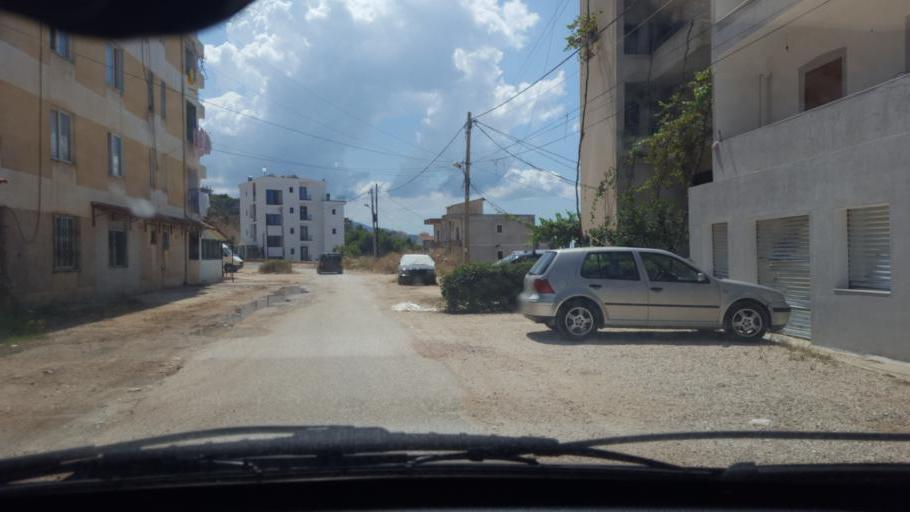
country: AL
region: Vlore
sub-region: Rrethi i Sarandes
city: Sarande
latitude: 39.8653
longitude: 20.0197
